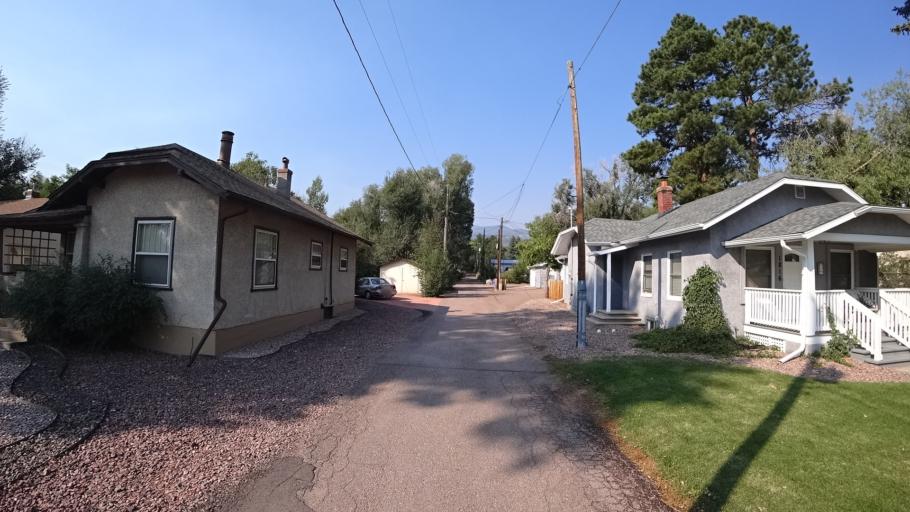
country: US
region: Colorado
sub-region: El Paso County
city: Colorado Springs
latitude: 38.8050
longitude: -104.8346
